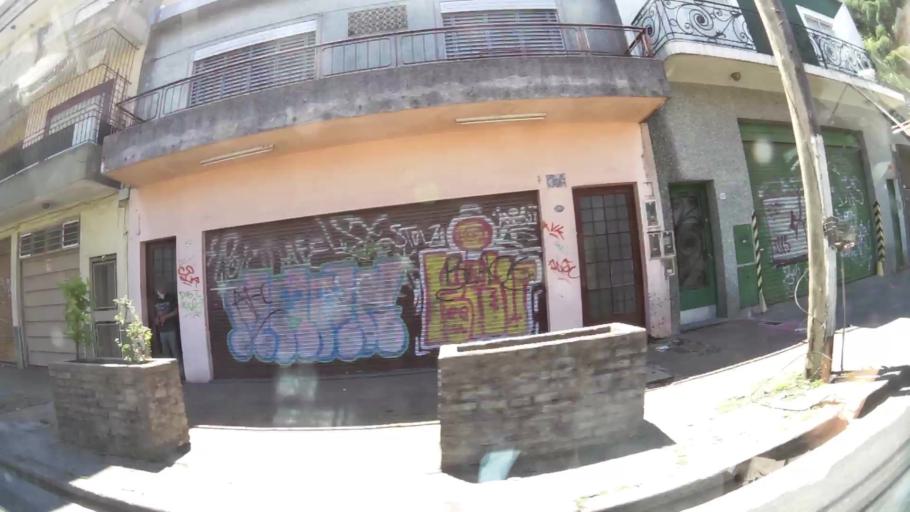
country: AR
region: Buenos Aires
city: Caseros
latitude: -34.6027
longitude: -58.5533
